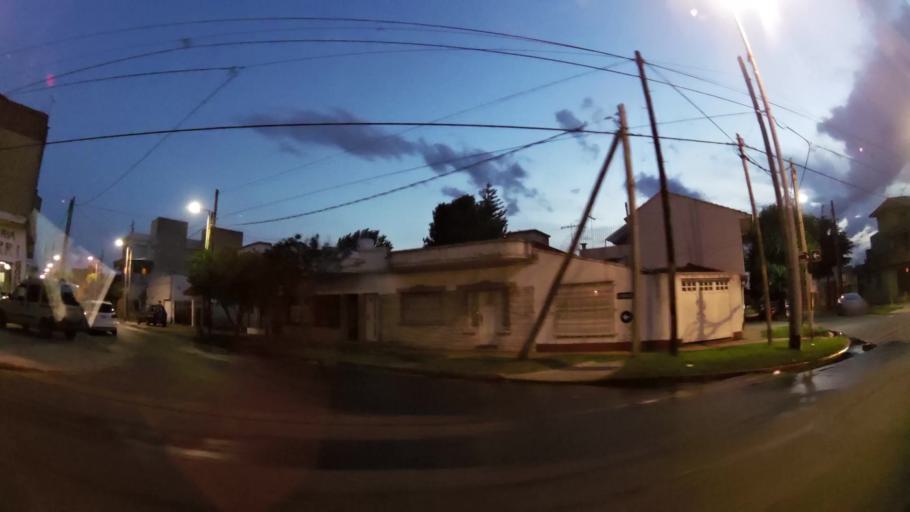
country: AR
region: Buenos Aires
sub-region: Partido de Avellaneda
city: Avellaneda
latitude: -34.6951
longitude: -58.3249
